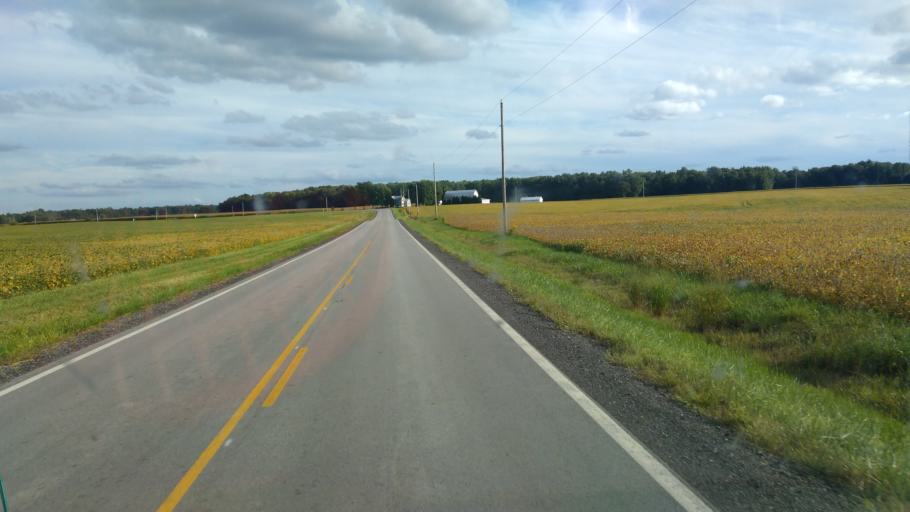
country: US
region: Ohio
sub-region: Crawford County
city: Bucyrus
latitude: 40.9249
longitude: -83.0488
